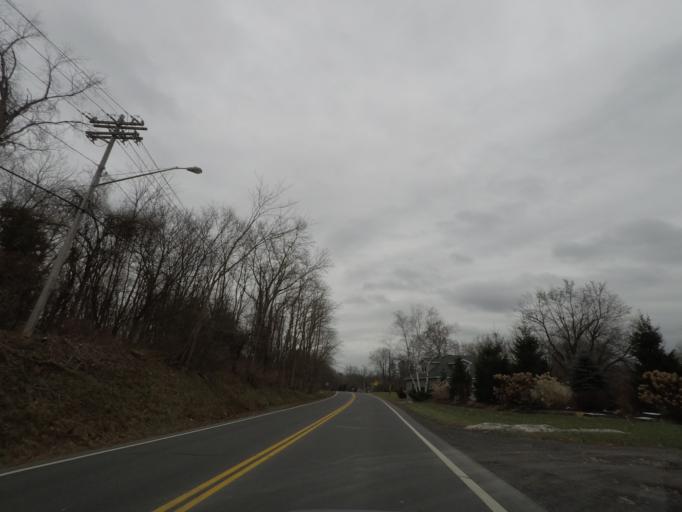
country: US
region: New York
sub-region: Schenectady County
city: Niskayuna
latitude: 42.7791
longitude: -73.8871
